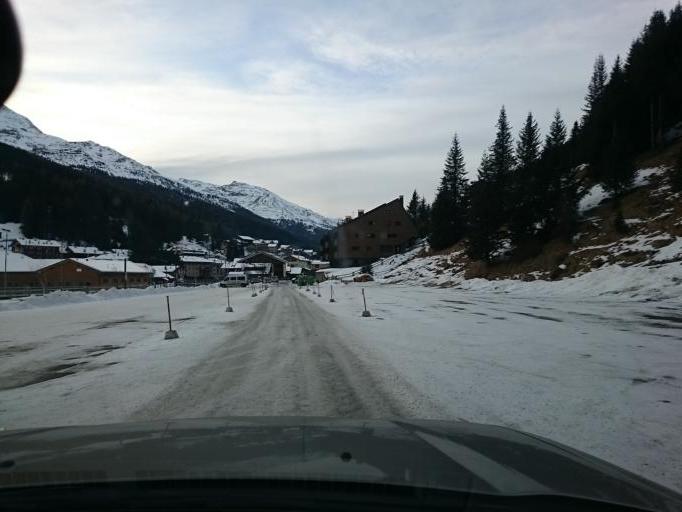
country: IT
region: Lombardy
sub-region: Provincia di Sondrio
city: Sant'Antonio
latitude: 46.4114
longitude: 10.4997
